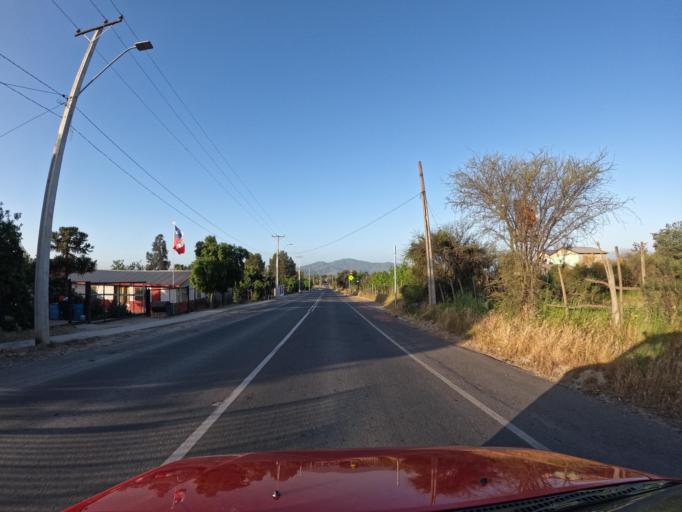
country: CL
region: O'Higgins
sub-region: Provincia de Colchagua
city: Santa Cruz
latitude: -34.3174
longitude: -71.3867
